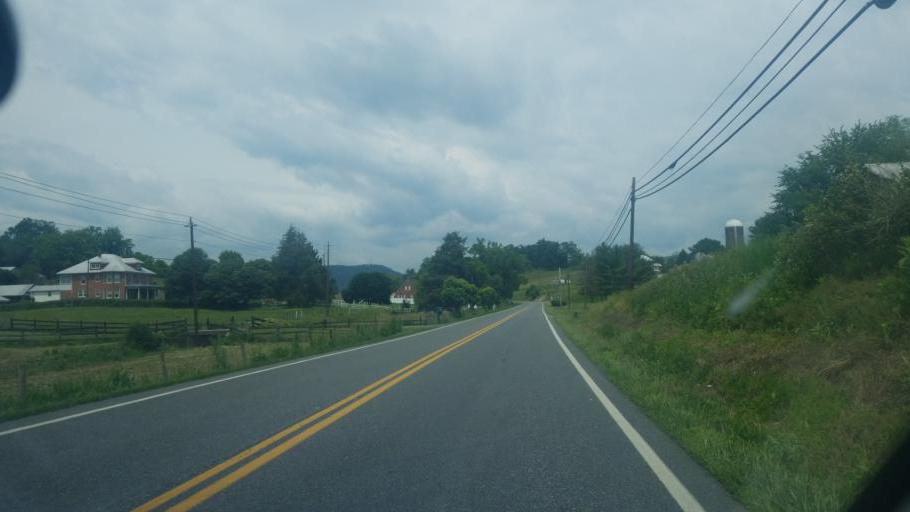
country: US
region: Virginia
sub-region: Rockingham County
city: Dayton
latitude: 38.4752
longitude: -78.9875
